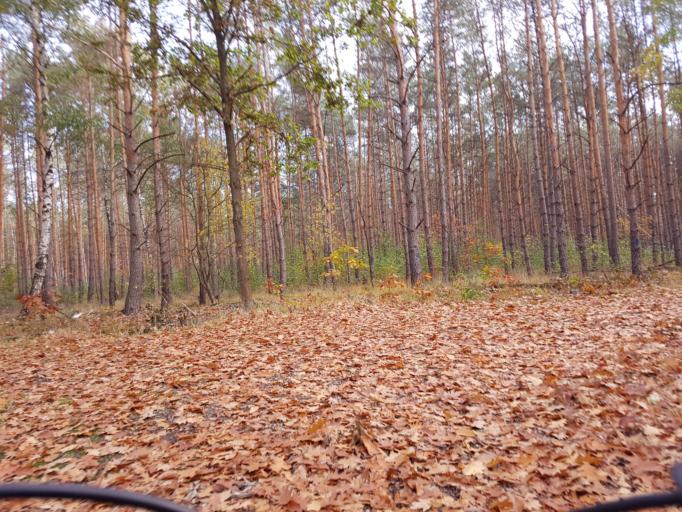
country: DE
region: Brandenburg
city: Schilda
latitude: 51.5871
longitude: 13.3457
